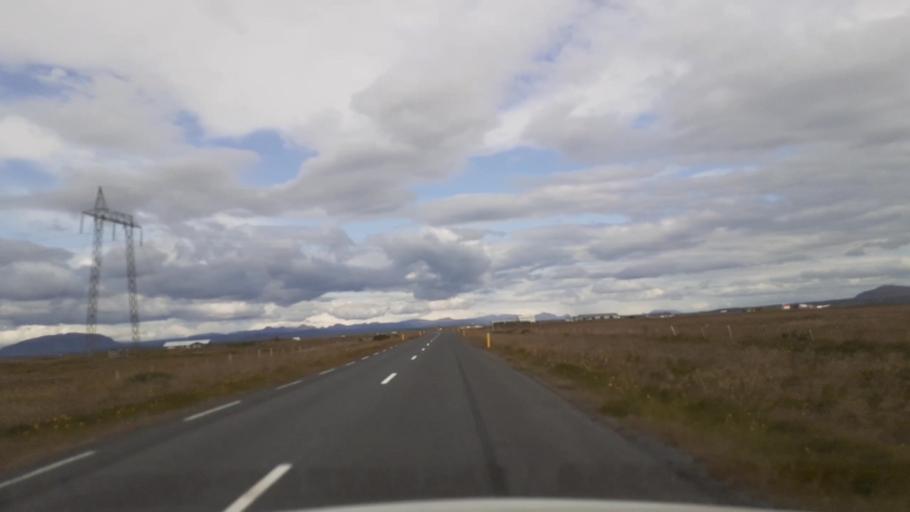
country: IS
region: South
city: Selfoss
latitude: 63.9382
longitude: -20.8397
